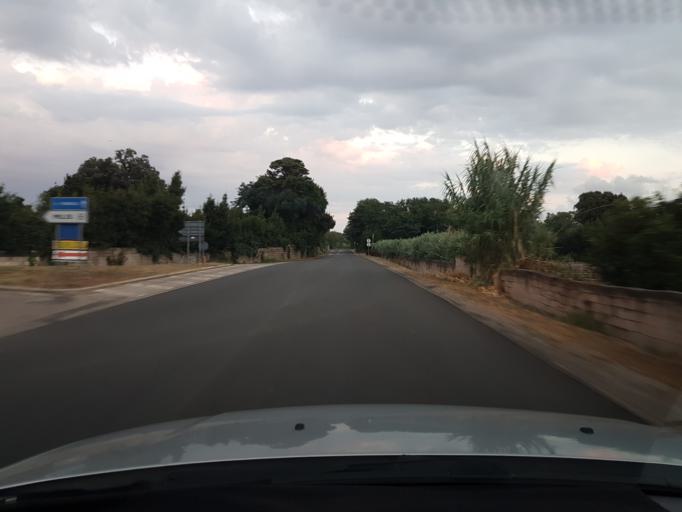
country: IT
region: Sardinia
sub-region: Provincia di Oristano
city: Milis
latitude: 40.0443
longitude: 8.6338
